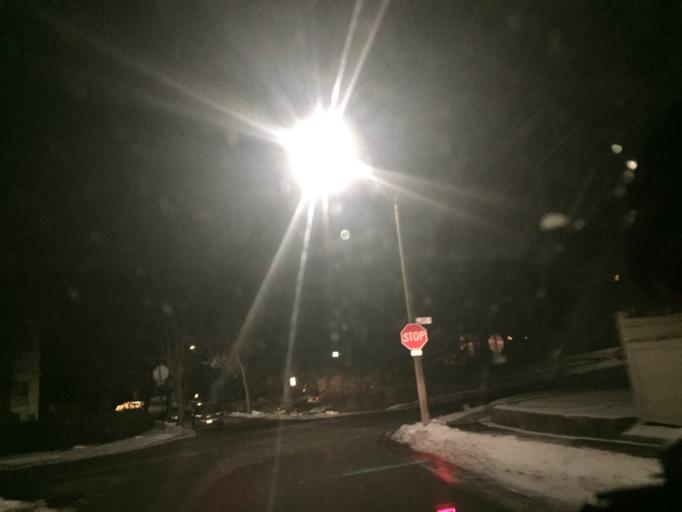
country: US
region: Massachusetts
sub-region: Norfolk County
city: Brookline
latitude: 42.3324
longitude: -71.1492
